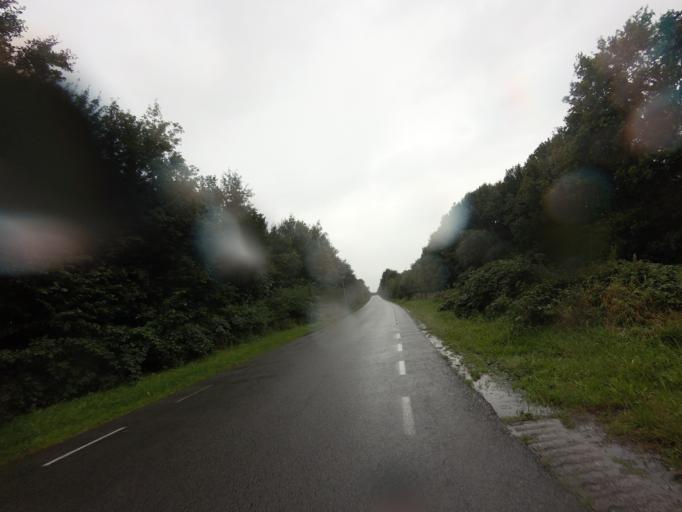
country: NL
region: Drenthe
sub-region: Gemeente Hoogeveen
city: Hoogeveen
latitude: 52.6437
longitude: 6.4408
